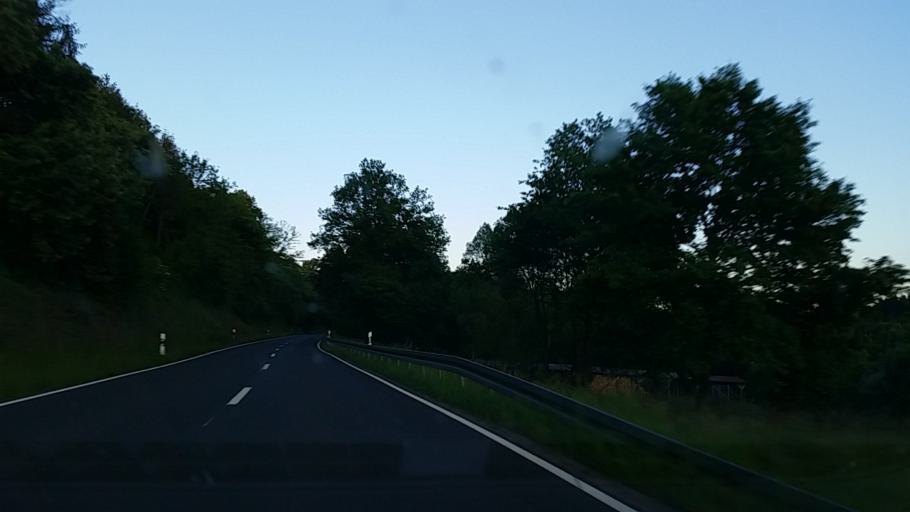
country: DE
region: Bavaria
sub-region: Regierungsbezirk Unterfranken
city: Burgsinn
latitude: 50.1673
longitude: 9.6467
